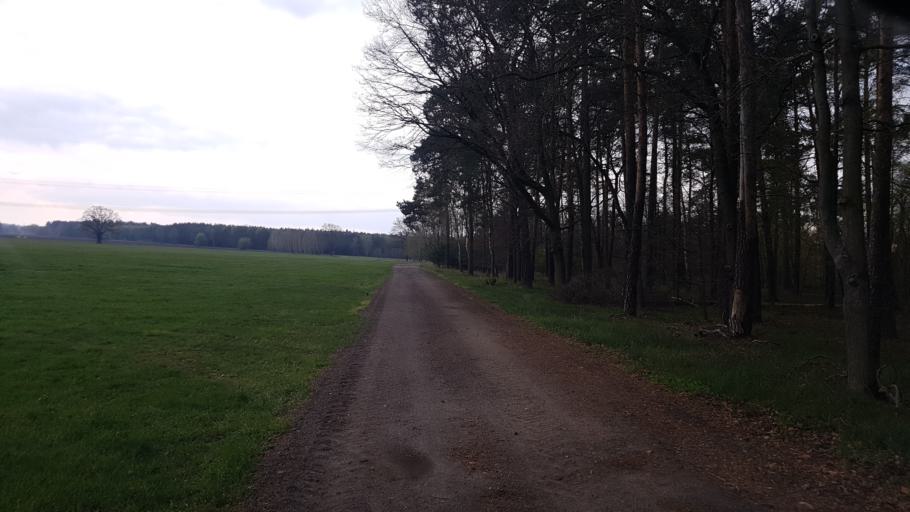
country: DE
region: Brandenburg
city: Bronkow
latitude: 51.6348
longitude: 13.8931
